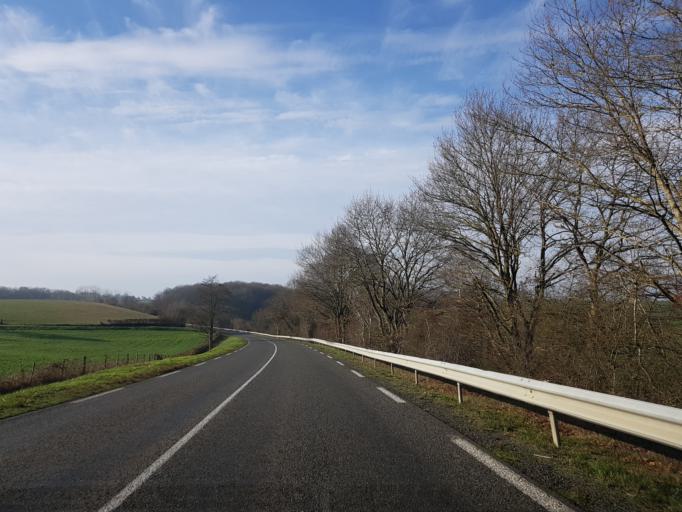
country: FR
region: Bourgogne
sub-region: Departement de Saone-et-Loire
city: La Motte-Saint-Jean
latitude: 46.6047
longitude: 3.9024
